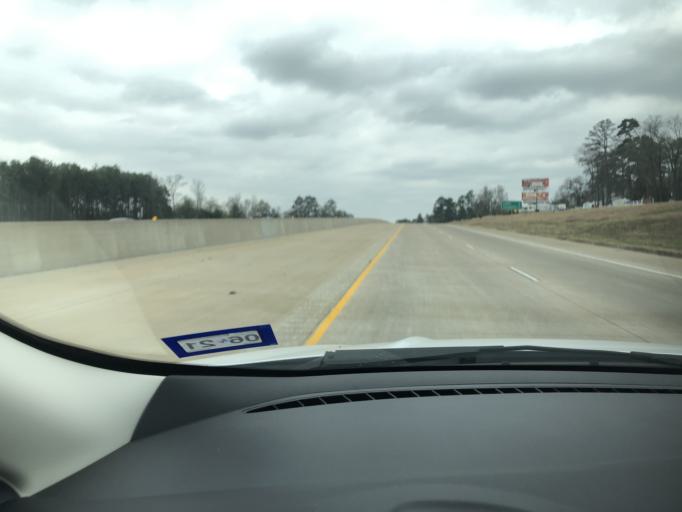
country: US
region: Texas
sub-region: Angelina County
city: Redland
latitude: 31.4095
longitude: -94.7205
